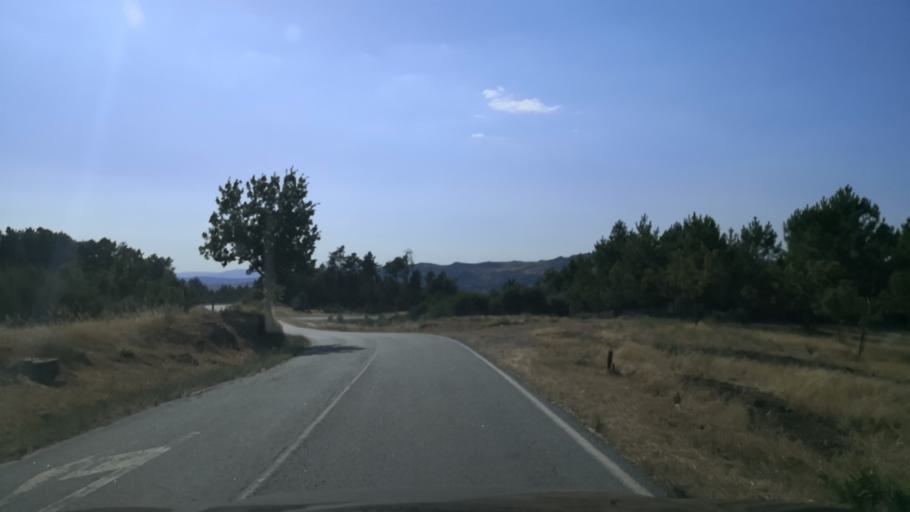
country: PT
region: Vila Real
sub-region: Murca
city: Murca
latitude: 41.3530
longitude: -7.4795
